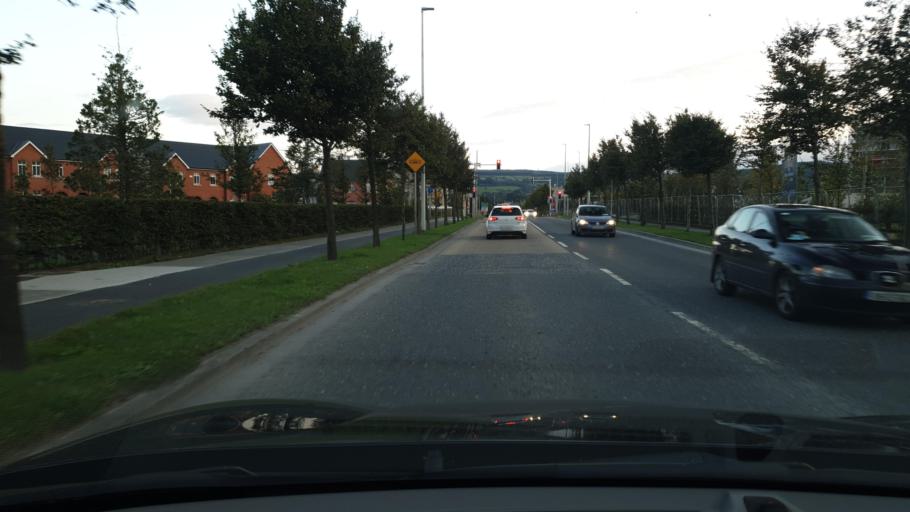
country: IE
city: Jobstown
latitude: 53.2864
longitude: -6.4219
